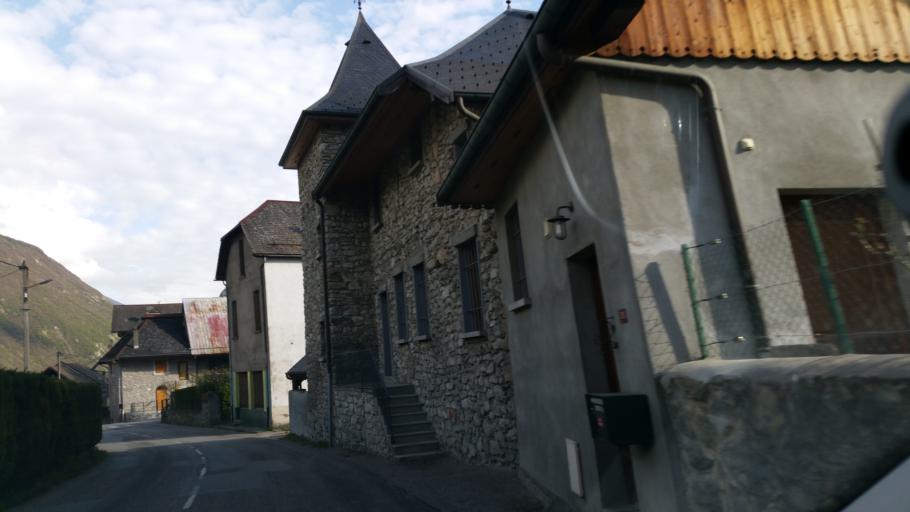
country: FR
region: Rhone-Alpes
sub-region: Departement de la Savoie
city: La Chambre
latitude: 45.3392
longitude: 6.3008
